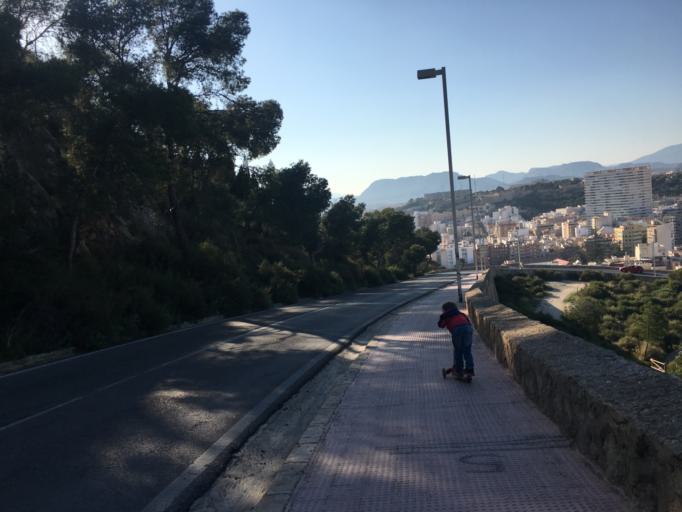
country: ES
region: Valencia
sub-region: Provincia de Alicante
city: Alicante
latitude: 38.3498
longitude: -0.4793
